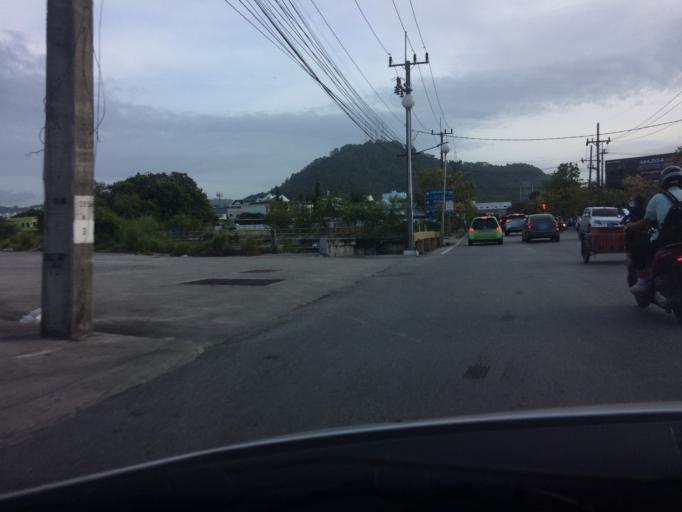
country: TH
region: Phuket
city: Ban Talat Yai
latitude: 7.8799
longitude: 98.3986
